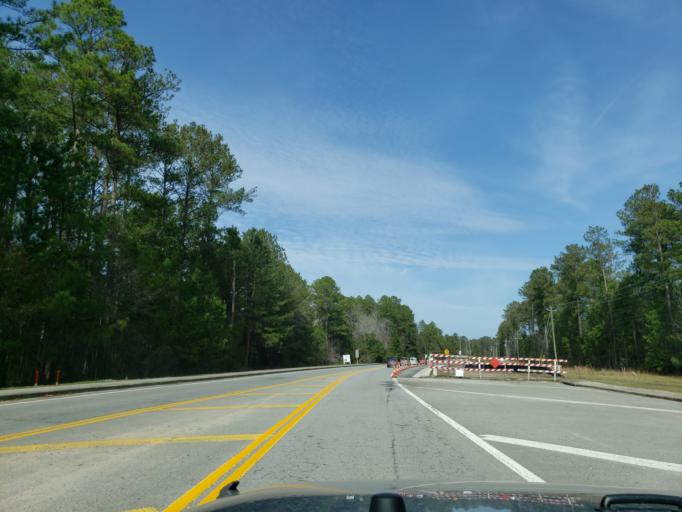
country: US
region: Georgia
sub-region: Chatham County
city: Pooler
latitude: 32.1681
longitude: -81.2341
